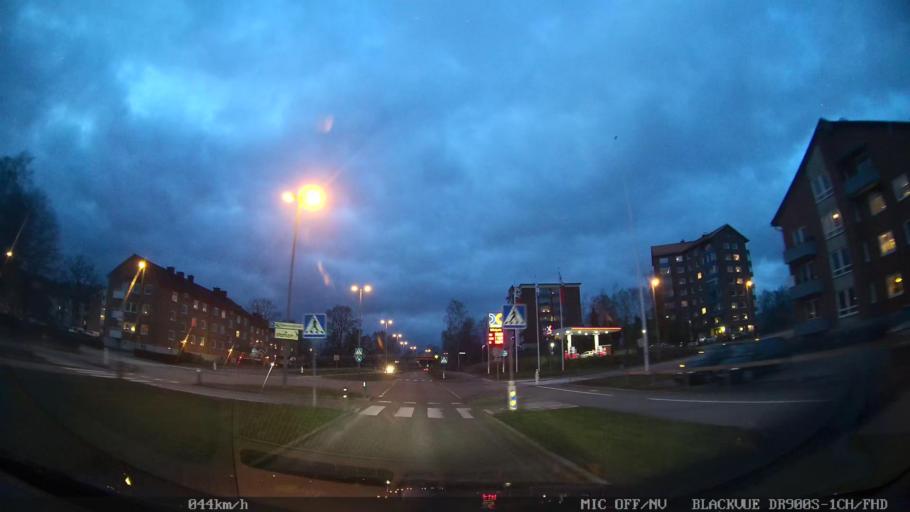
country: SE
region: Skane
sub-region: Hassleholms Kommun
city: Hassleholm
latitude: 56.1577
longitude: 13.7555
